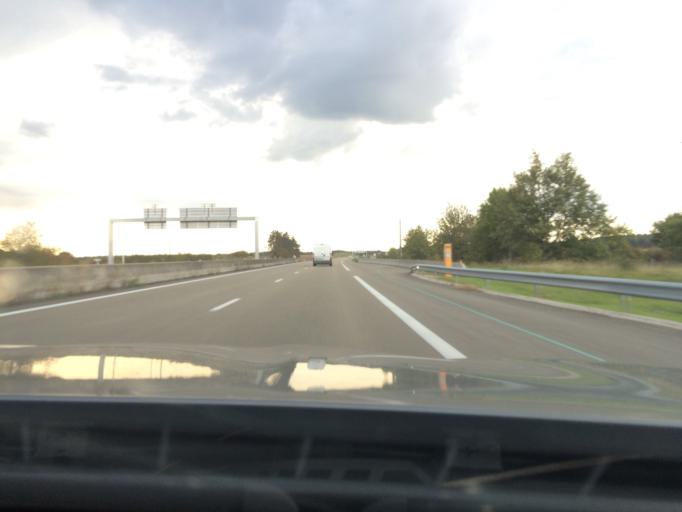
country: FR
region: Ile-de-France
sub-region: Departement de Seine-et-Marne
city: Souppes-sur-Loing
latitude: 48.2211
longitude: 2.7684
